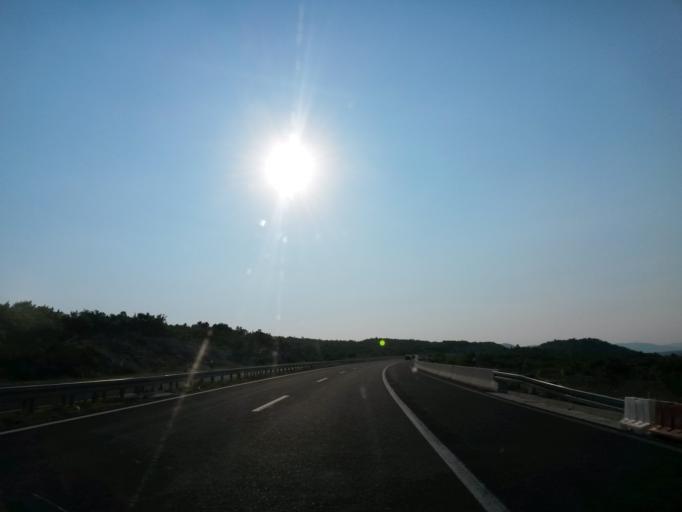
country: HR
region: Splitsko-Dalmatinska
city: Dugopolje
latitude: 43.5825
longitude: 16.6476
